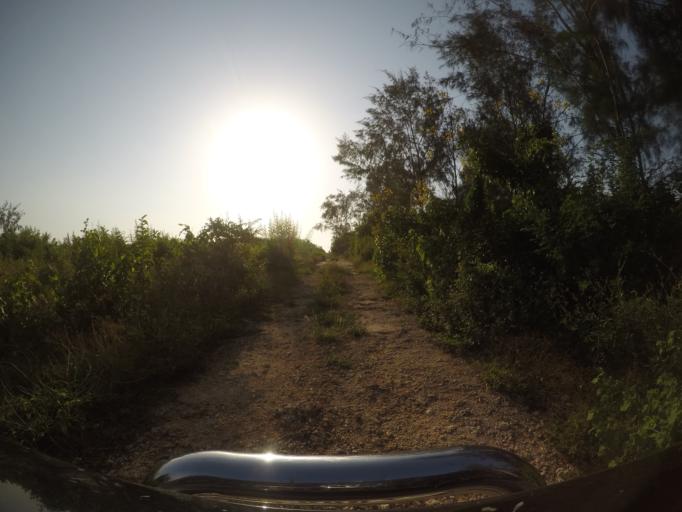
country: TZ
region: Zanzibar Central/South
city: Nganane
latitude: -6.2094
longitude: 39.5321
